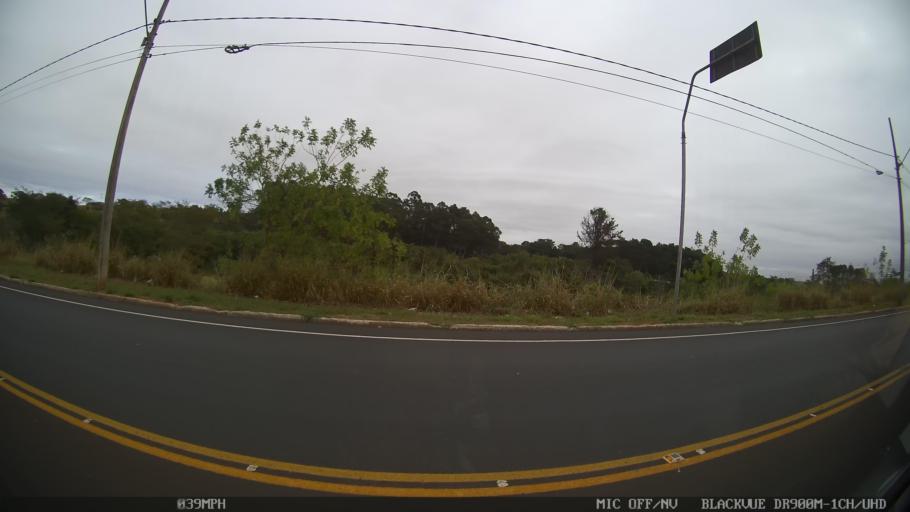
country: BR
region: Sao Paulo
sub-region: Sao Jose Do Rio Preto
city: Sao Jose do Rio Preto
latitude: -20.8197
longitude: -49.4353
